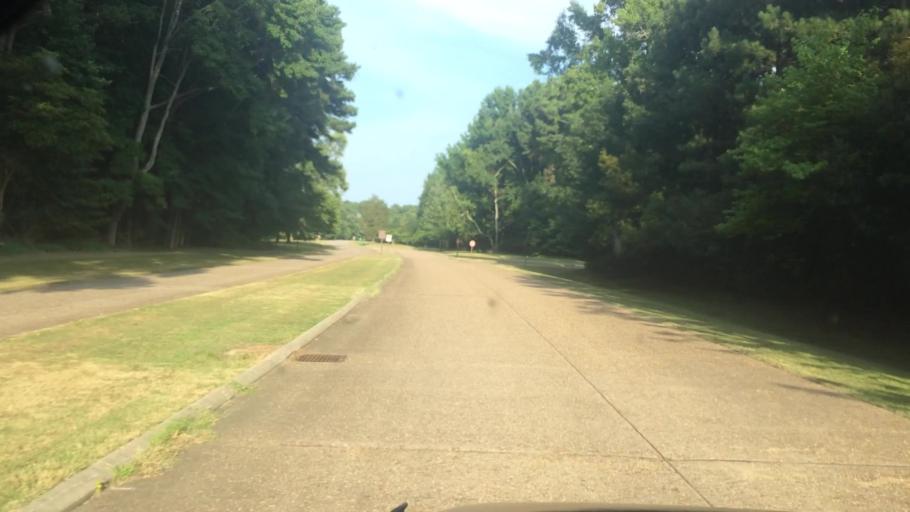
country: US
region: Virginia
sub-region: James City County
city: Williamsburg
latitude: 37.2208
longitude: -76.7713
